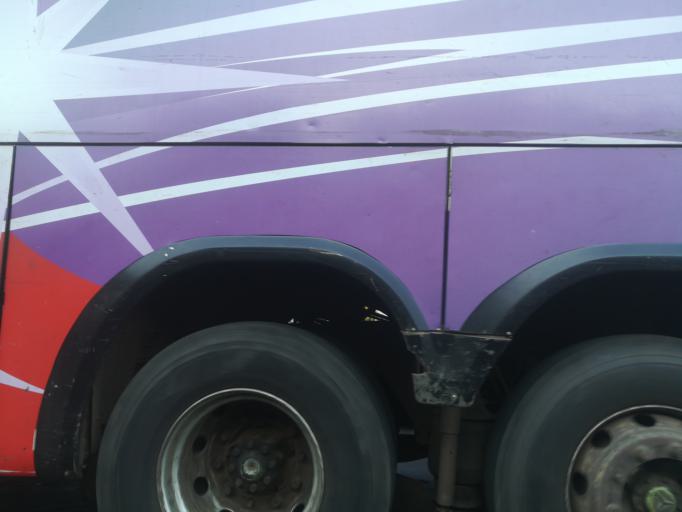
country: NG
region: Abuja Federal Capital Territory
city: Abuja
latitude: 9.0676
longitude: 7.4523
